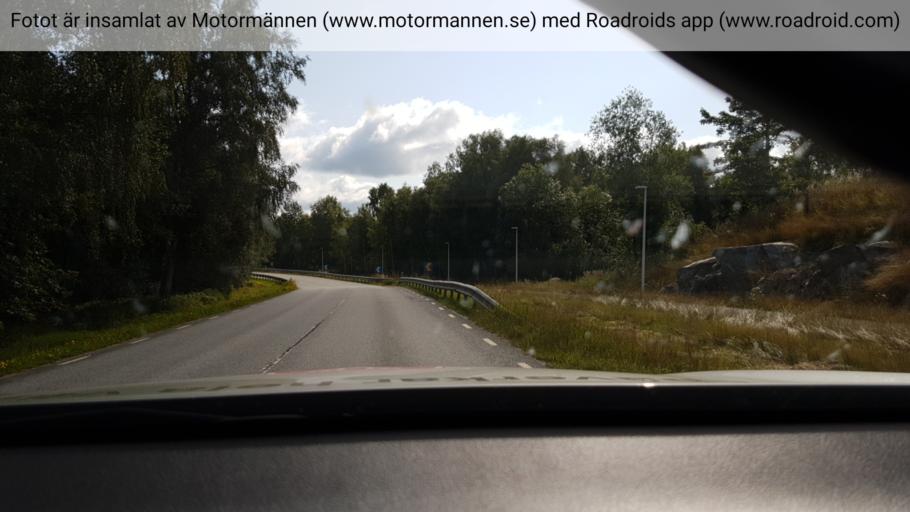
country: SE
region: Uppsala
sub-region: Knivsta Kommun
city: Knivsta
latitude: 59.7142
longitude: 17.7621
